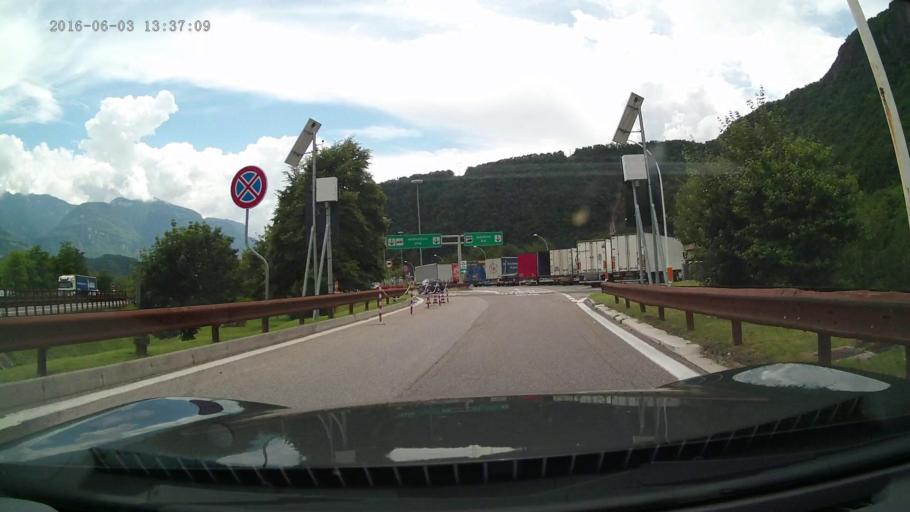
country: IT
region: Trentino-Alto Adige
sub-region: Bolzano
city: Ora
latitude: 46.3617
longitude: 11.2890
